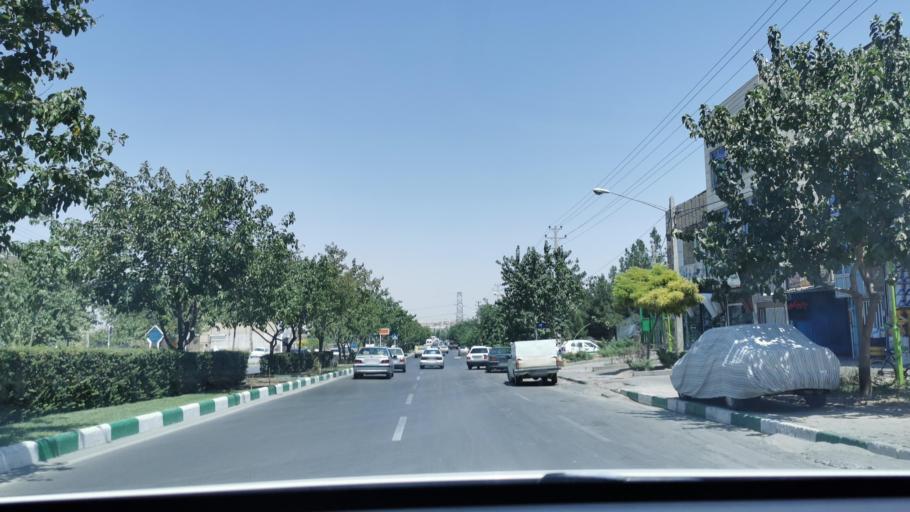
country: IR
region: Razavi Khorasan
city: Mashhad
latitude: 36.3473
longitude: 59.6274
